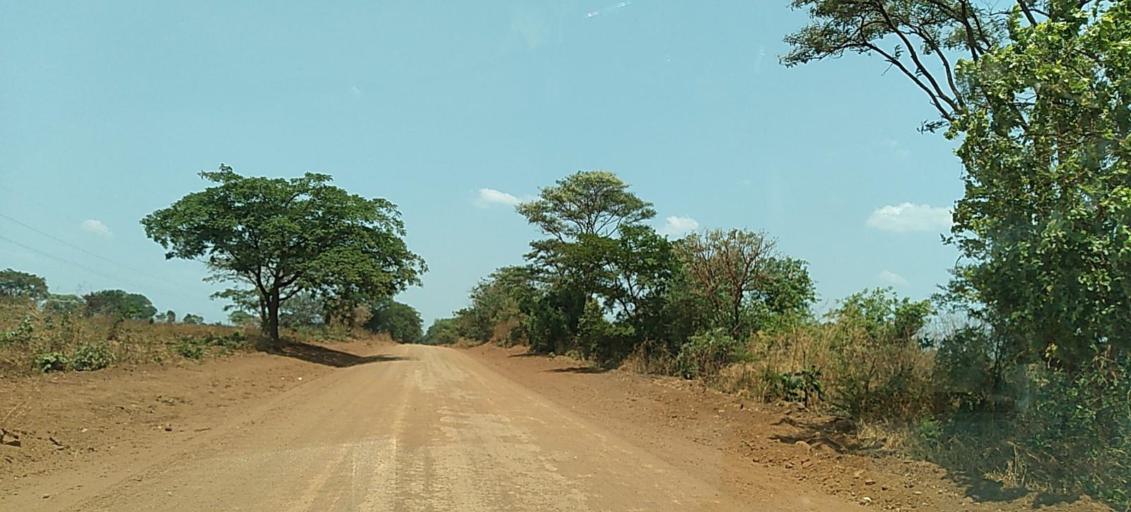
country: ZM
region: Copperbelt
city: Mpongwe
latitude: -13.5169
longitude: 27.9903
